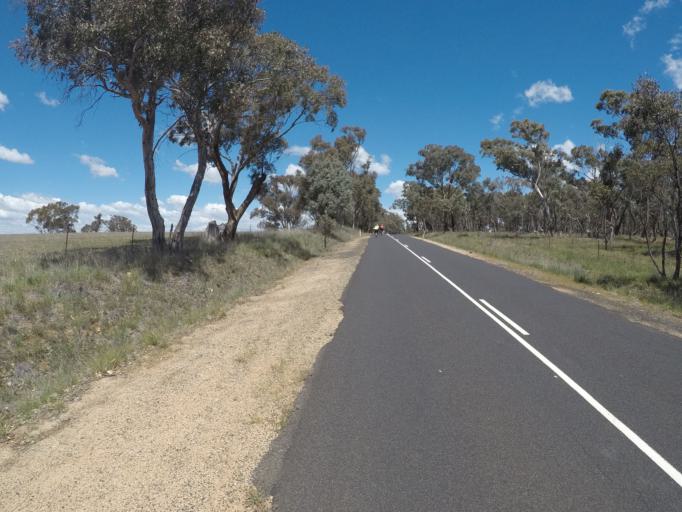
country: AU
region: New South Wales
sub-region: Bathurst Regional
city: Perthville
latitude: -33.5391
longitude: 149.4390
